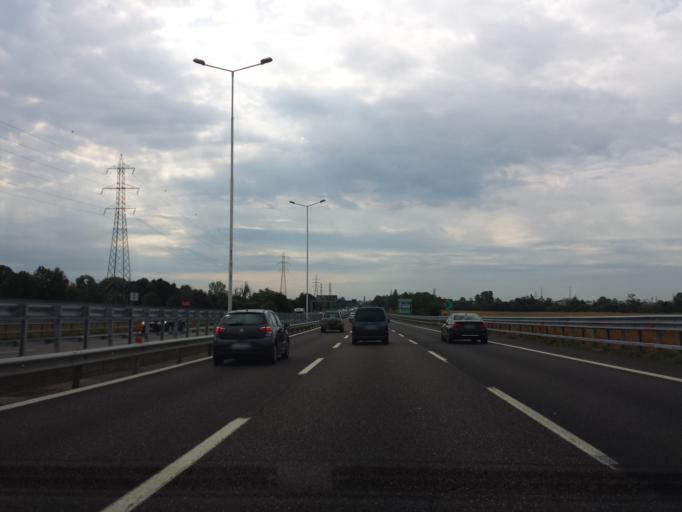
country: IT
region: Lombardy
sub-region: Citta metropolitana di Milano
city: Figino
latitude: 45.4852
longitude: 9.0690
